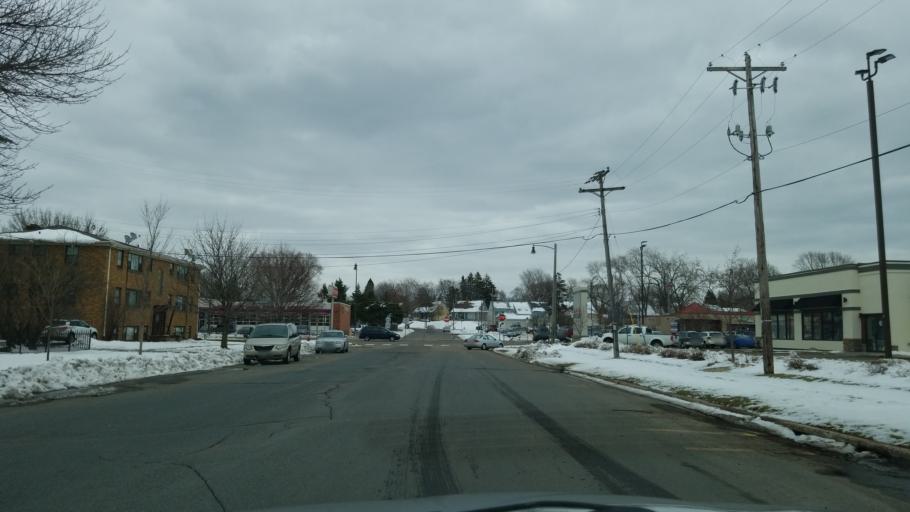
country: US
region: Minnesota
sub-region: Dakota County
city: West Saint Paul
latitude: 44.9105
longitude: -93.0818
